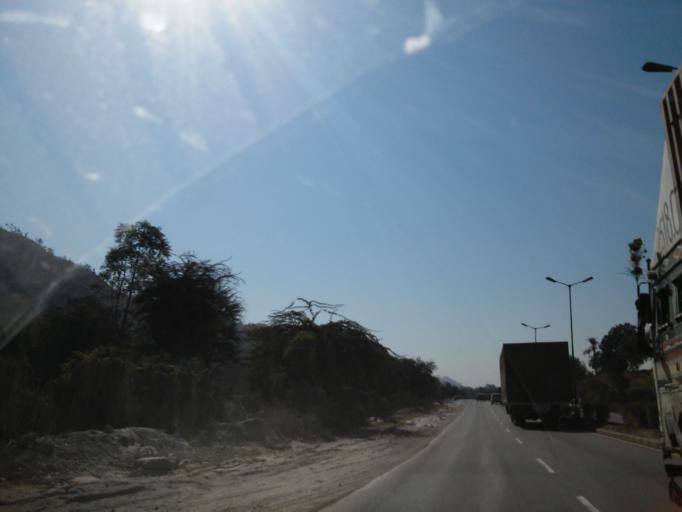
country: IN
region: Rajasthan
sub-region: Udaipur
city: Udaipur
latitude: 24.2685
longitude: 73.6743
